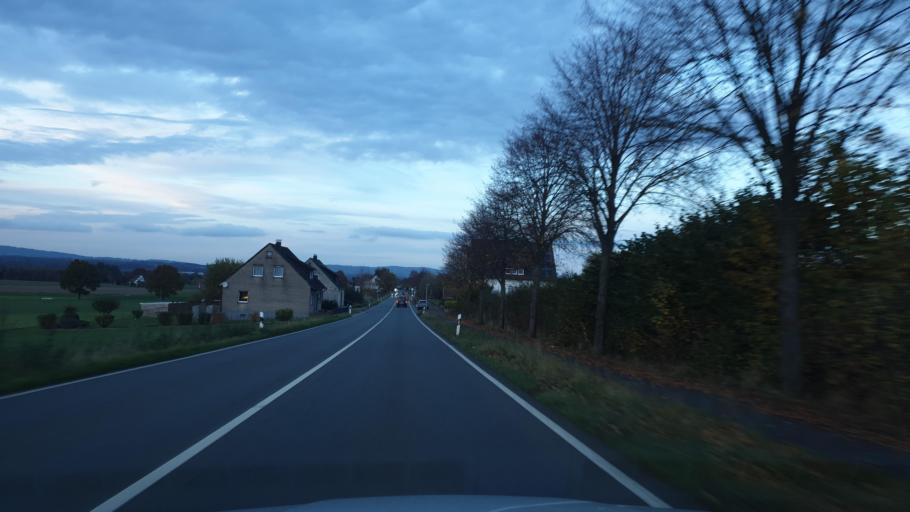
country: DE
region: North Rhine-Westphalia
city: Spenge
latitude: 52.1651
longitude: 8.5038
